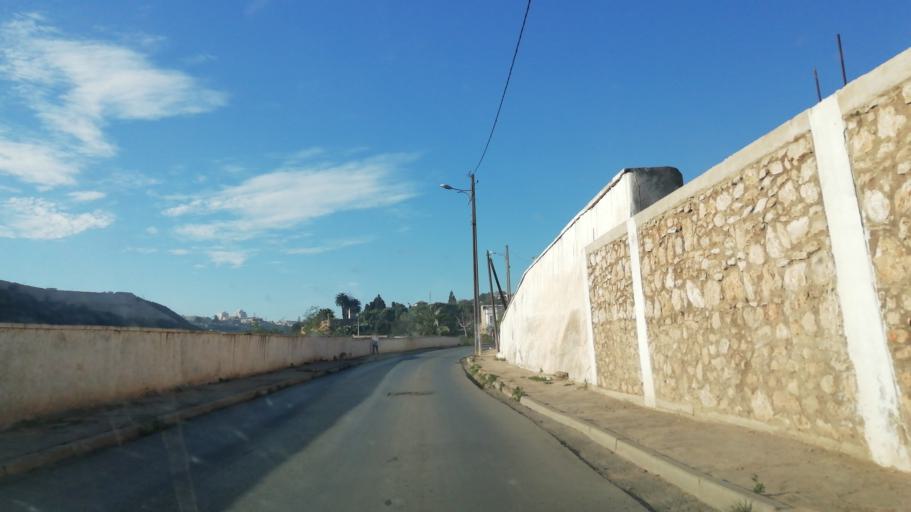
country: DZ
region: Oran
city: Oran
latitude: 35.6993
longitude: -0.6558
